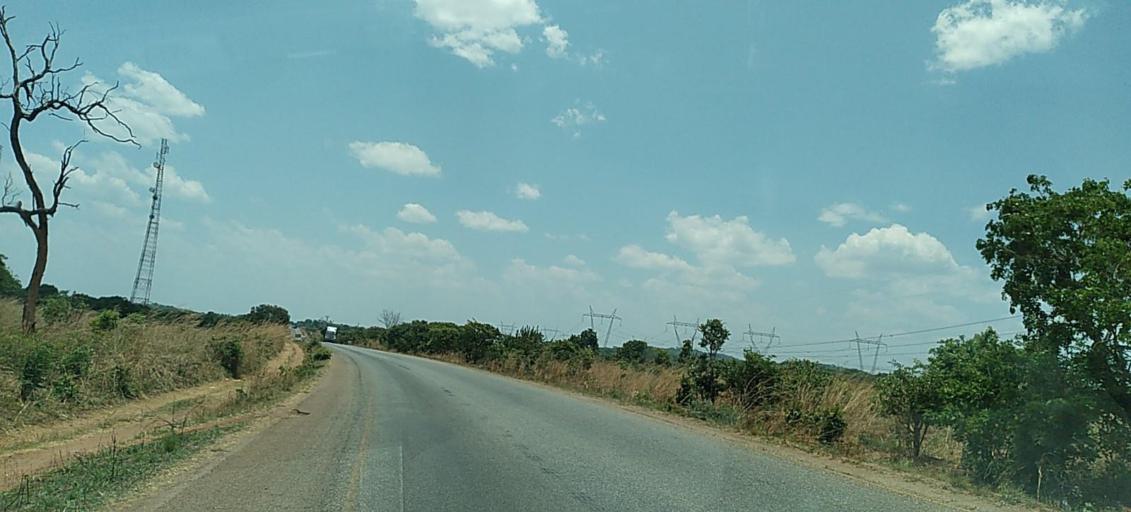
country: ZM
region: Central
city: Kapiri Mposhi
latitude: -13.6967
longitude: 28.6280
